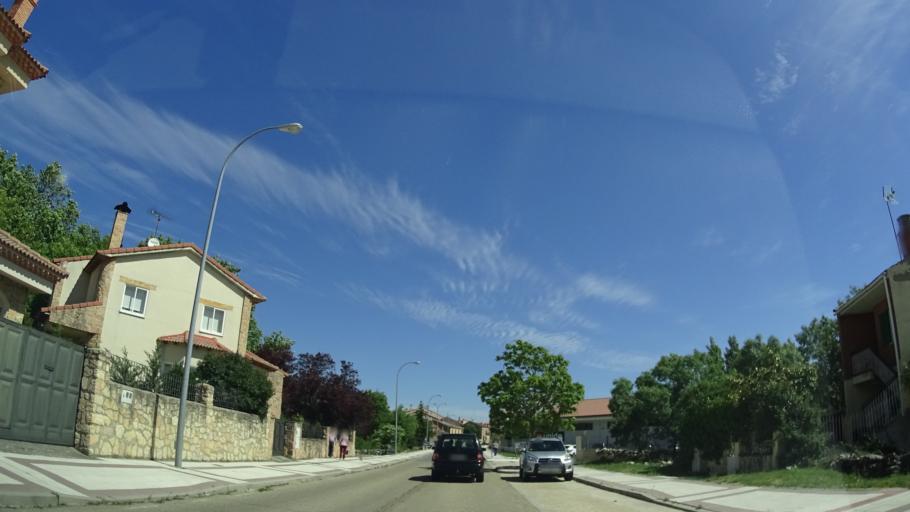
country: ES
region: Castille and Leon
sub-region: Provincia de Segovia
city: Pradena
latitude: 41.1352
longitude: -3.6884
